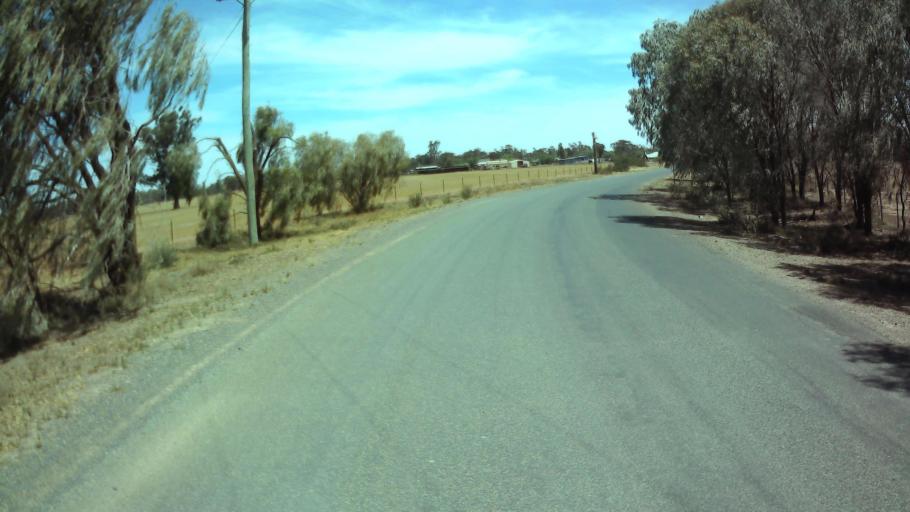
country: AU
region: New South Wales
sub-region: Weddin
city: Grenfell
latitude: -33.8368
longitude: 147.7466
